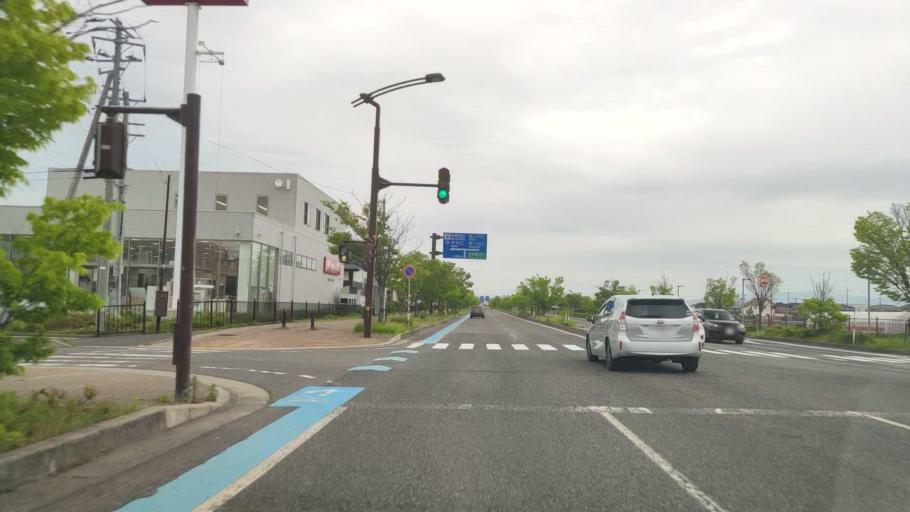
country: JP
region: Niigata
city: Kameda-honcho
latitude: 37.8834
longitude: 139.0678
